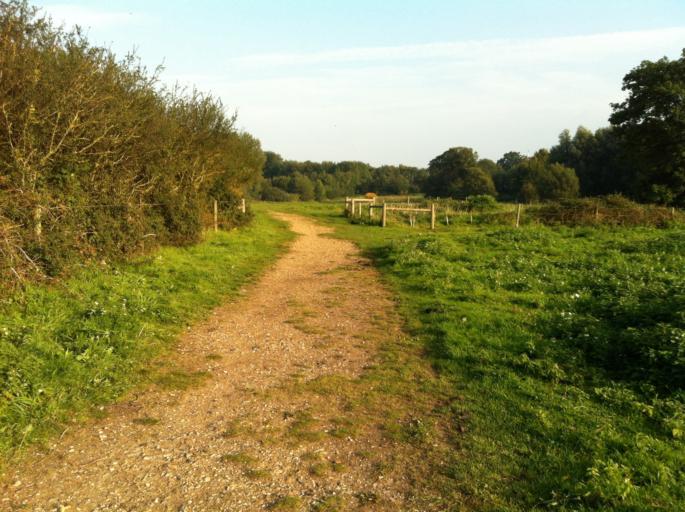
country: GB
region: England
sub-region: Norfolk
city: Bowthorpe
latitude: 52.6274
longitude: 1.2162
